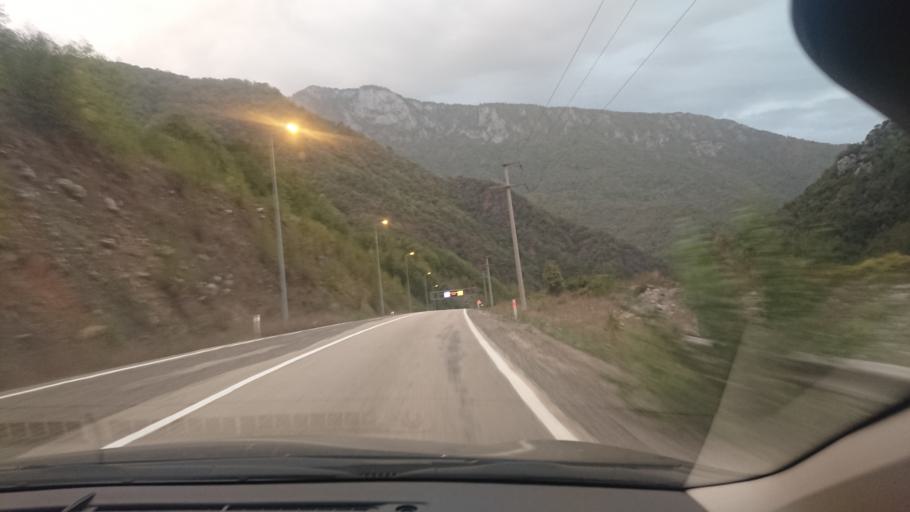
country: TR
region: Karabuk
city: Yenice
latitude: 41.1570
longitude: 32.4682
